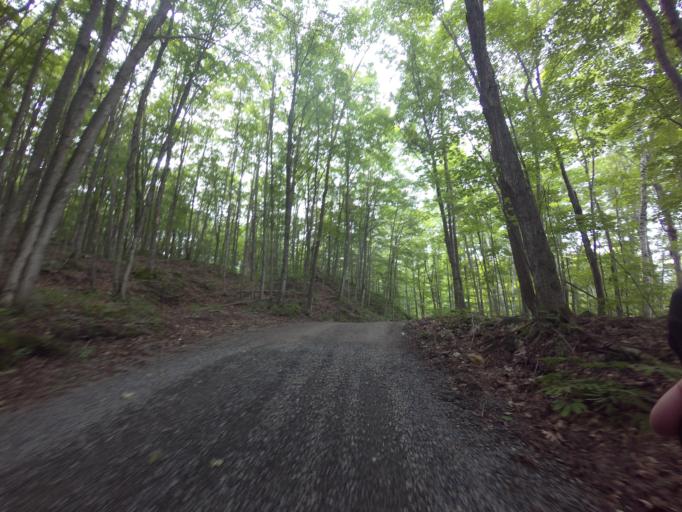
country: CA
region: Ontario
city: Kingston
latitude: 44.5637
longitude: -76.5663
